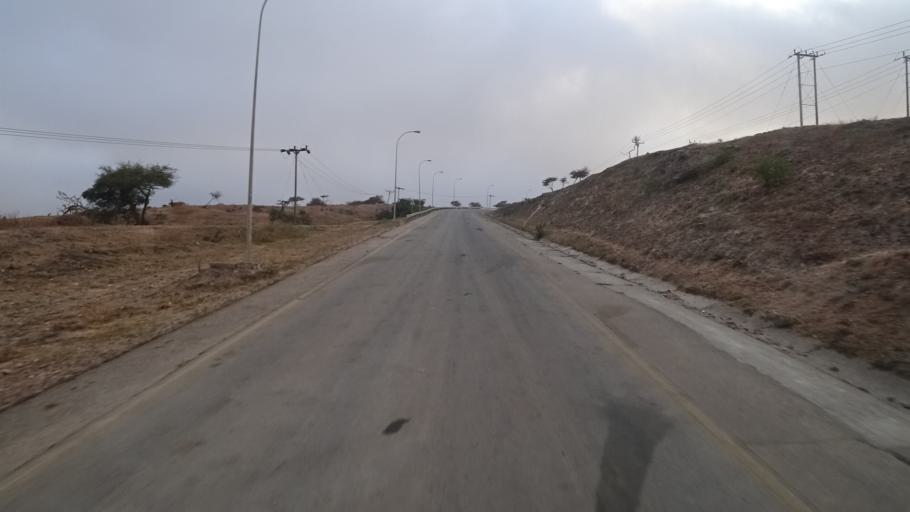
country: OM
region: Zufar
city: Salalah
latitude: 17.1388
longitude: 53.9672
